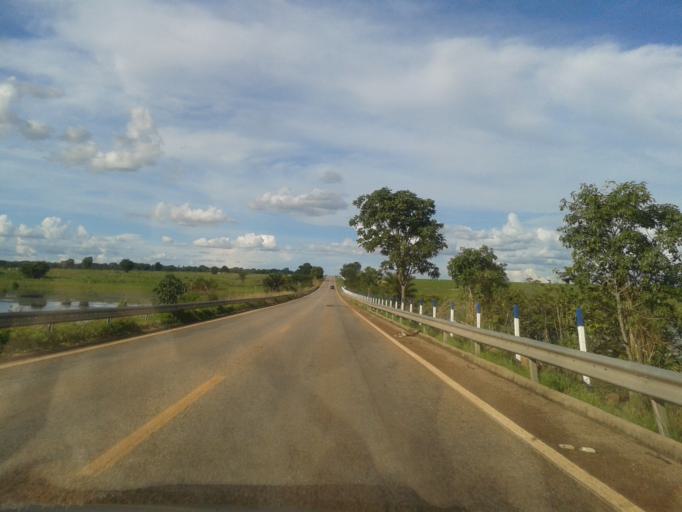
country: BR
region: Goias
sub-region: Mozarlandia
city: Mozarlandia
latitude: -14.3458
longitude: -50.4203
